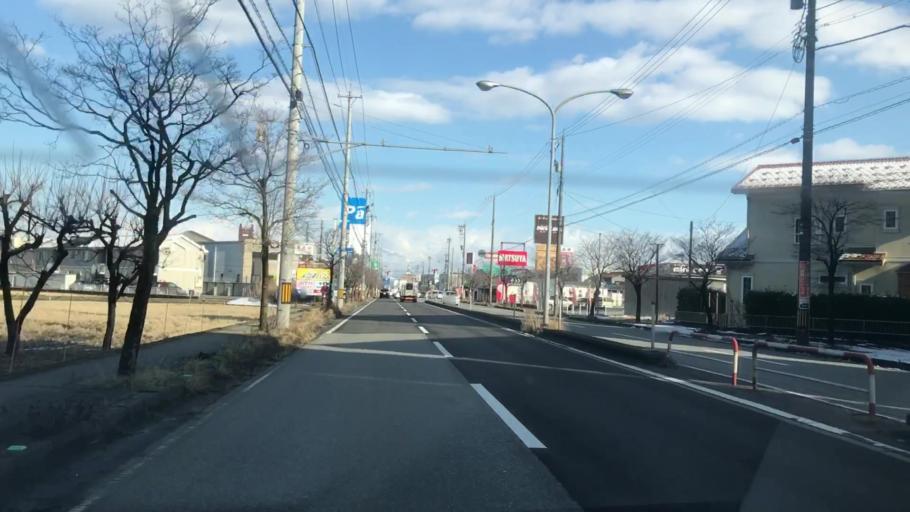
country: JP
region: Toyama
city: Toyama-shi
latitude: 36.6672
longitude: 137.2155
